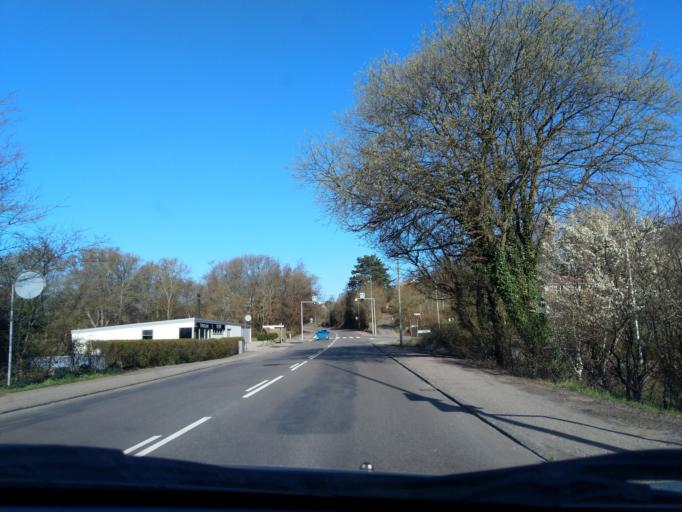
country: DK
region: Zealand
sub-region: Kalundborg Kommune
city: Kalundborg
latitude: 55.6983
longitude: 11.0394
